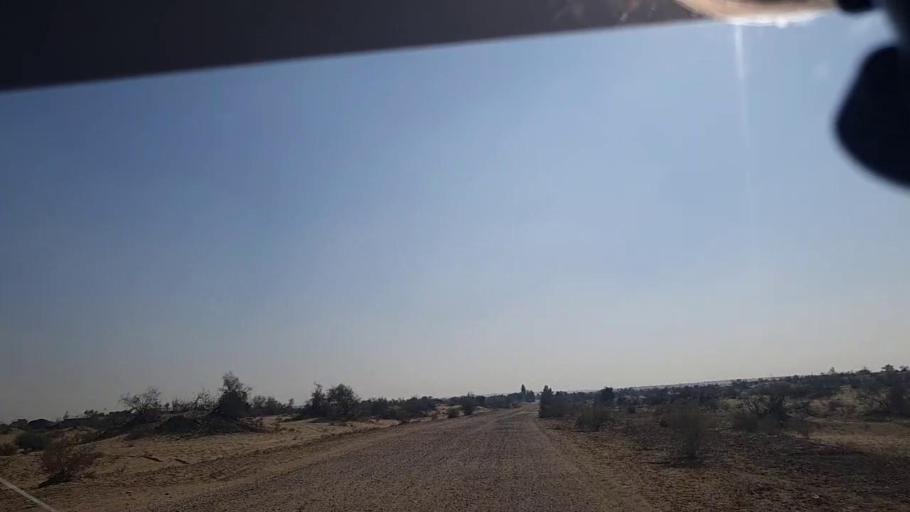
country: PK
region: Sindh
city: Khanpur
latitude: 27.5723
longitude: 69.3054
